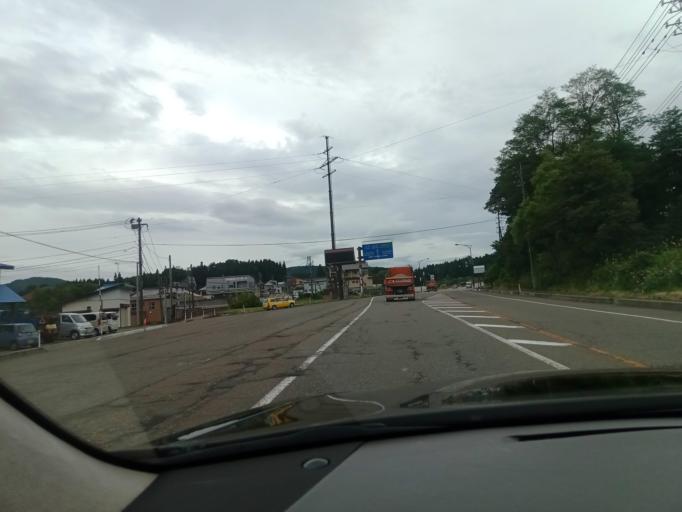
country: JP
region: Niigata
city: Arai
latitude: 36.8793
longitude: 138.2049
